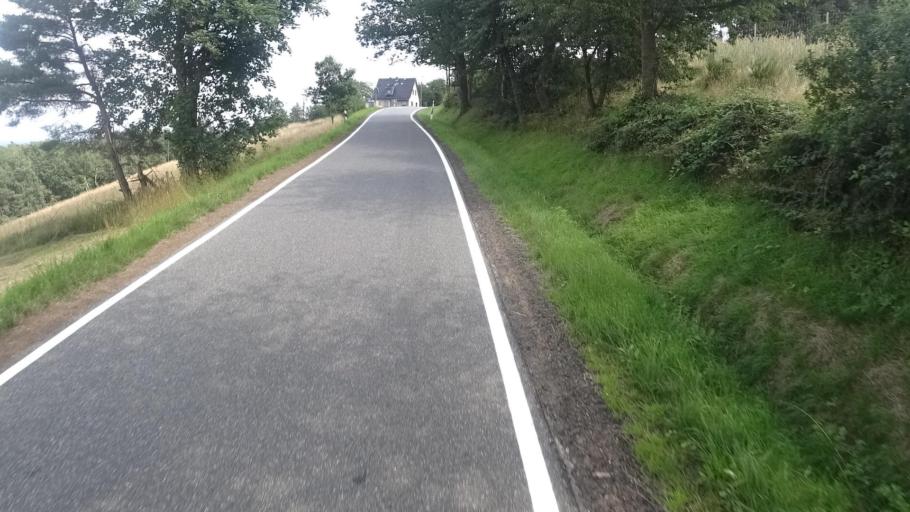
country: DE
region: Rheinland-Pfalz
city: Sankt Katharinen
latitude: 50.5845
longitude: 7.3620
